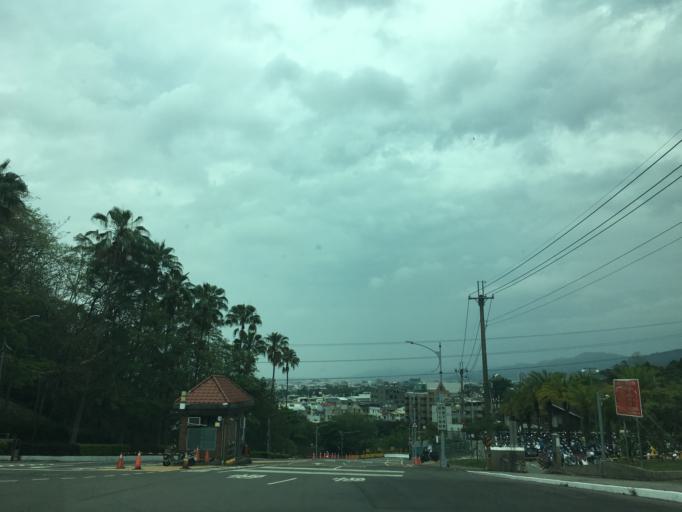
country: TW
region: Taiwan
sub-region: Taichung City
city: Taichung
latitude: 24.0704
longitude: 120.7157
